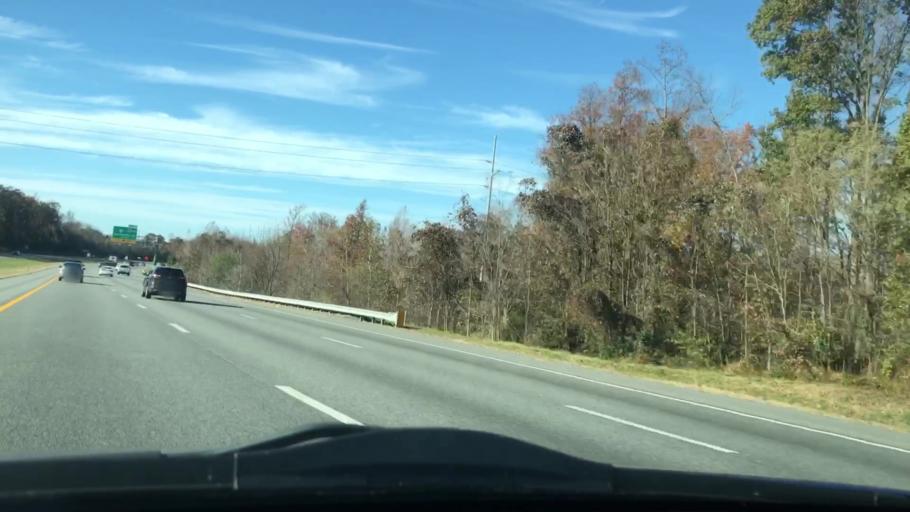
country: US
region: North Carolina
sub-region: Guilford County
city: High Point
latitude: 35.9903
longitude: -79.9816
